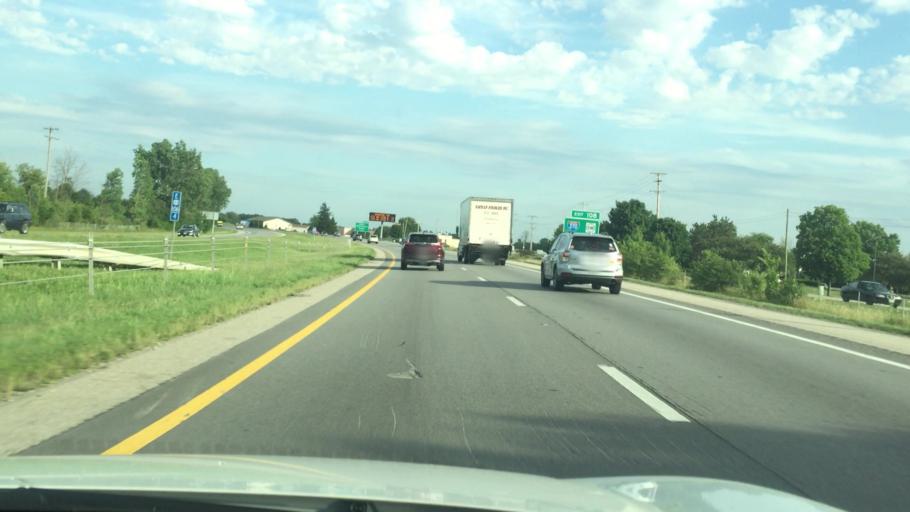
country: US
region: Ohio
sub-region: Franklin County
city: Dublin
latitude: 40.1049
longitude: -83.1773
